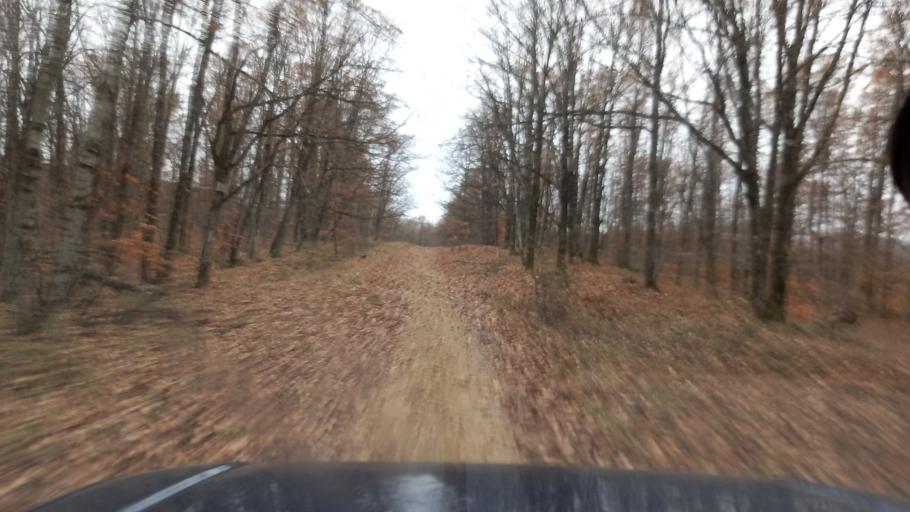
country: RU
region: Krasnodarskiy
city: Goryachiy Klyuch
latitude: 44.5026
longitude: 39.2832
